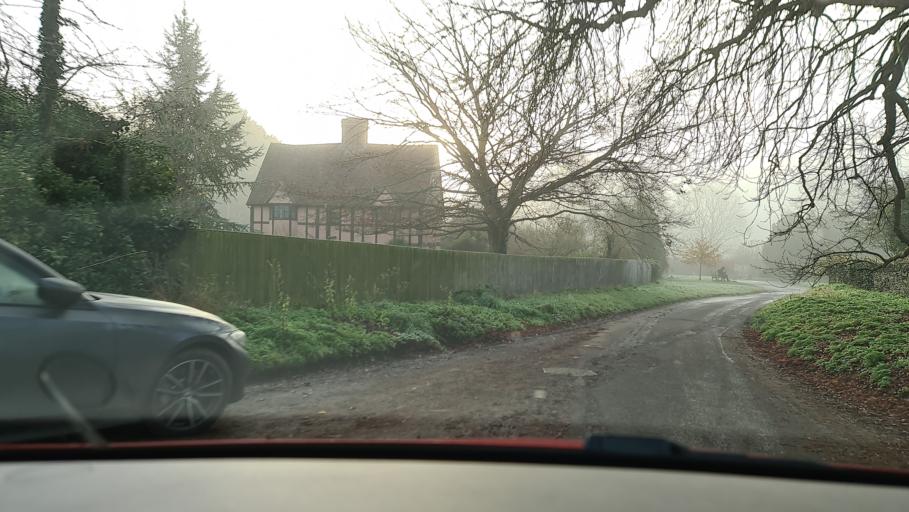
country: GB
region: England
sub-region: Buckinghamshire
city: Haddenham
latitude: 51.8045
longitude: -0.9384
